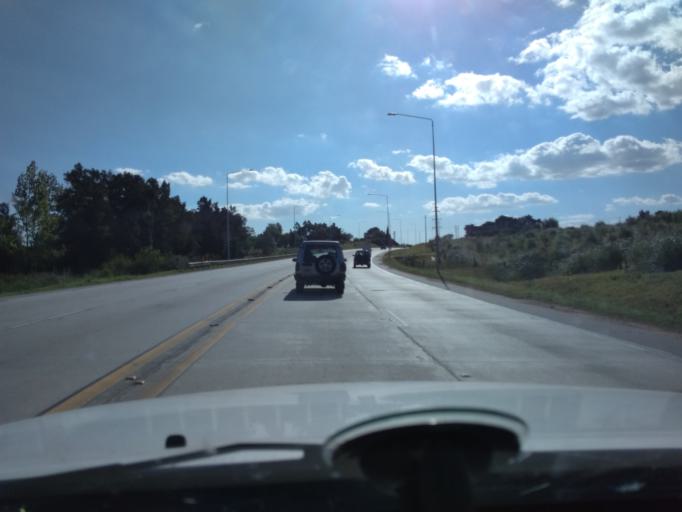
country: UY
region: Canelones
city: La Paz
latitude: -34.7829
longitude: -56.2464
